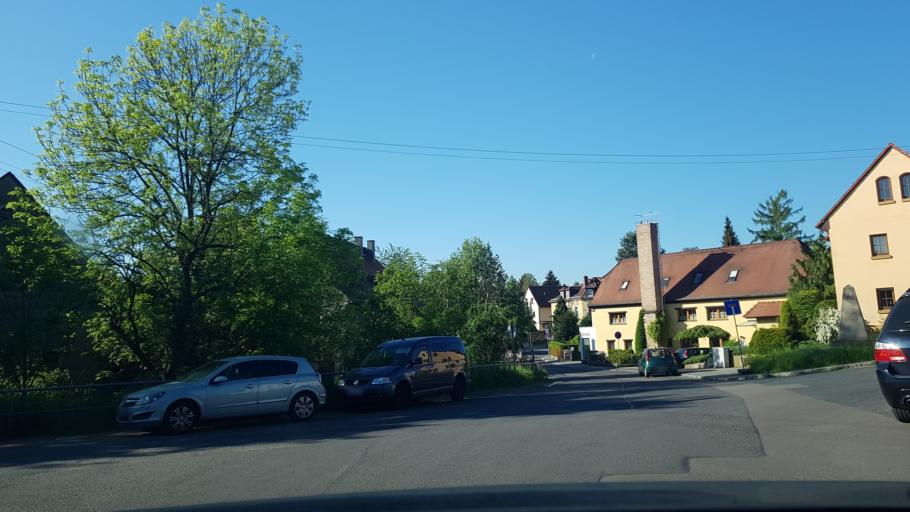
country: DE
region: Saxony
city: Kreischa
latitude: 50.9952
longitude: 13.7885
